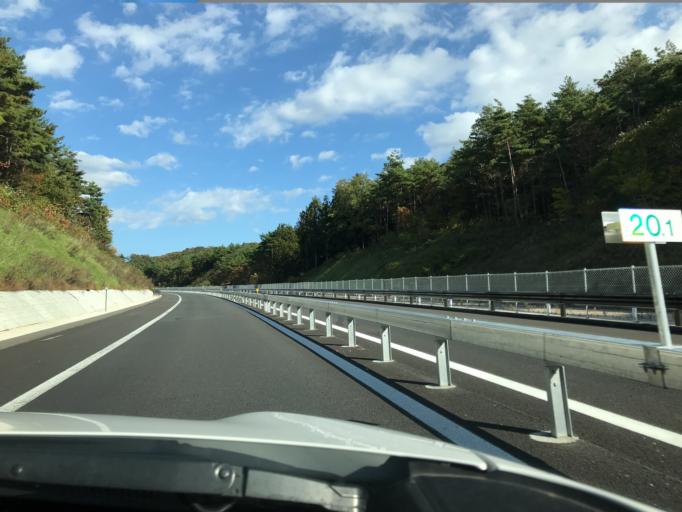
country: JP
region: Fukushima
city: Yanagawamachi-saiwaicho
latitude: 37.7557
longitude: 140.7227
